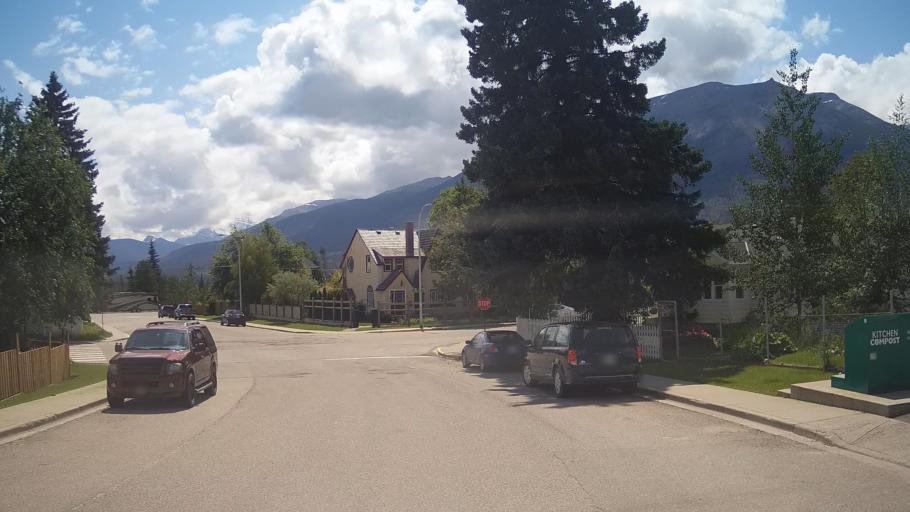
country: CA
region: Alberta
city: Jasper Park Lodge
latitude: 52.8725
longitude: -118.0870
